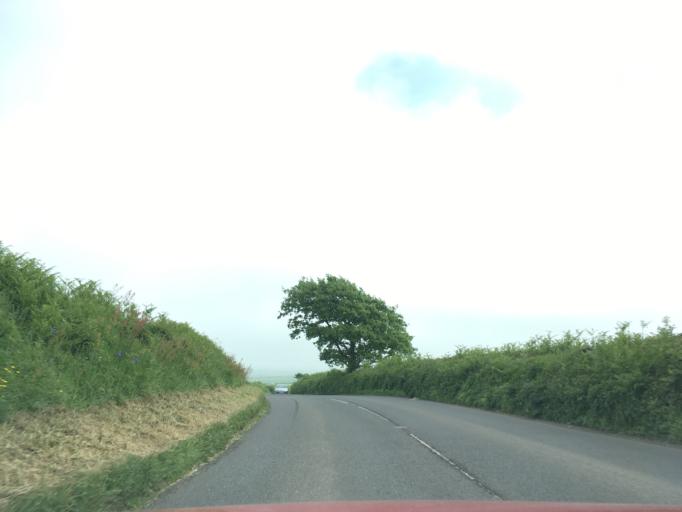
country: GB
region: England
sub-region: Devon
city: Dartmouth
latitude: 50.3563
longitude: -3.6411
